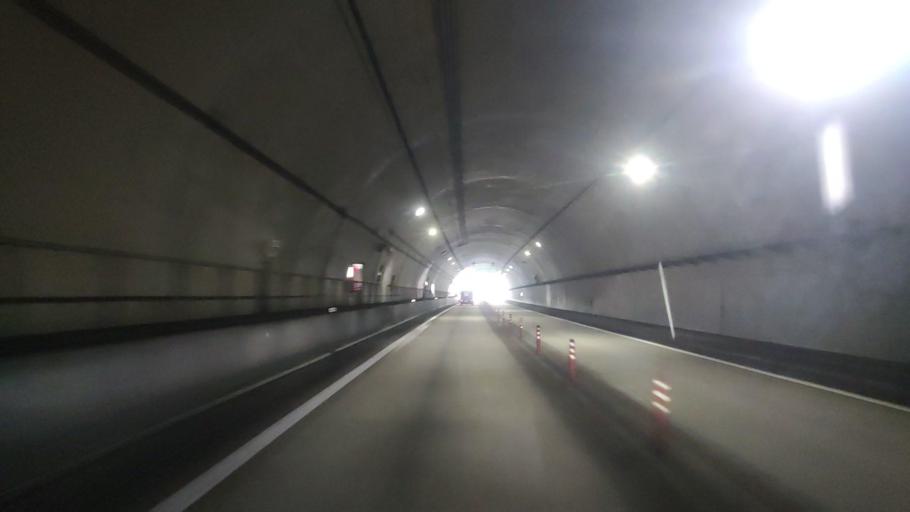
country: JP
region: Wakayama
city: Tanabe
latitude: 33.5522
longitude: 135.5129
